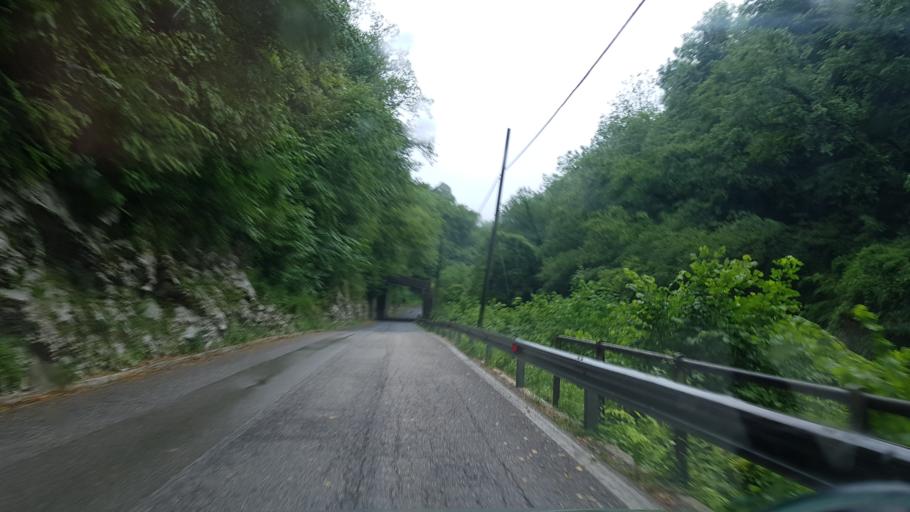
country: IT
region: Friuli Venezia Giulia
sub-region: Provincia di Udine
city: Nimis
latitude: 46.2337
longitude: 13.2849
